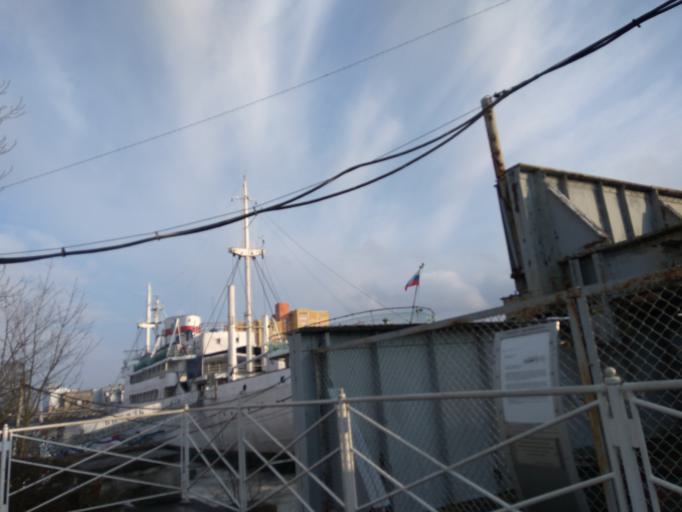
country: RU
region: Kaliningrad
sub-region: Gorod Kaliningrad
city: Kaliningrad
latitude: 54.7065
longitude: 20.4987
